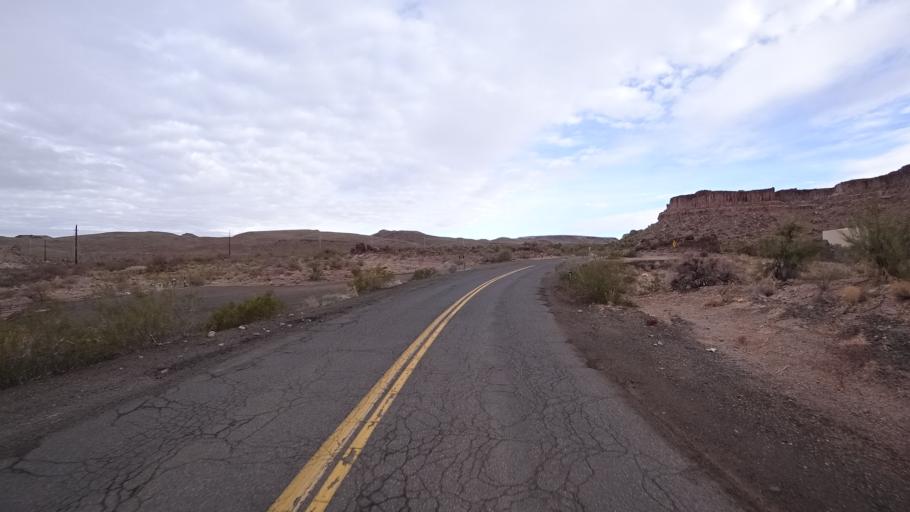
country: US
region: Arizona
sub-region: Mohave County
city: Kingman
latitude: 35.2033
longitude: -114.0811
